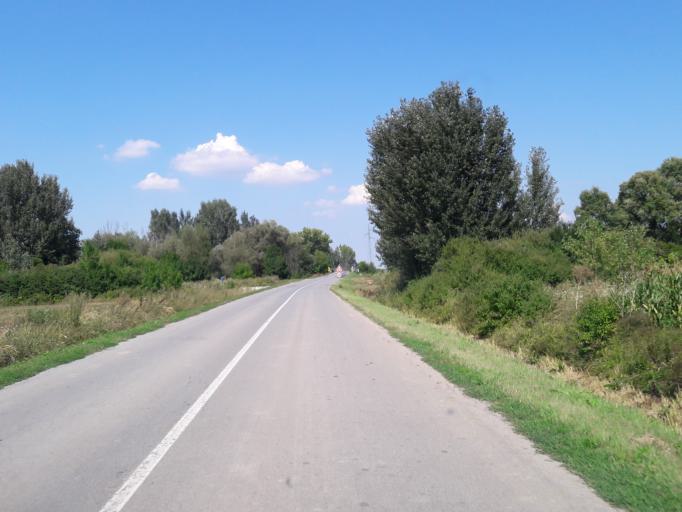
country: HR
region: Osjecko-Baranjska
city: Ernestinovo
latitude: 45.4341
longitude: 18.6463
